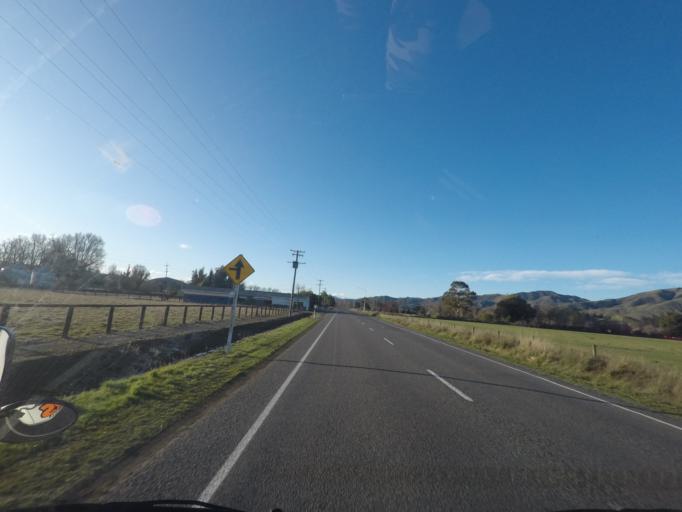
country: NZ
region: Canterbury
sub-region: Kaikoura District
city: Kaikoura
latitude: -42.7143
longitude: 173.2899
